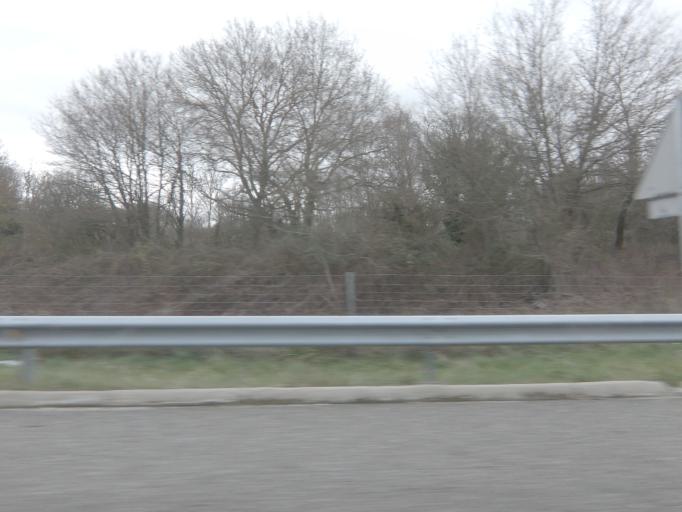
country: ES
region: Galicia
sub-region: Provincia de Ourense
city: Trasmiras
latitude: 42.0183
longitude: -7.6211
